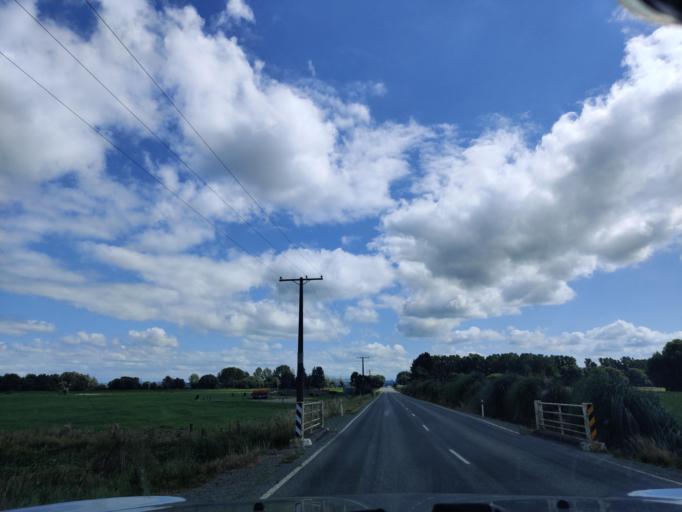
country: NZ
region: Canterbury
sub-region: Timaru District
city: Pleasant Point
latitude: -44.1264
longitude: 171.2643
